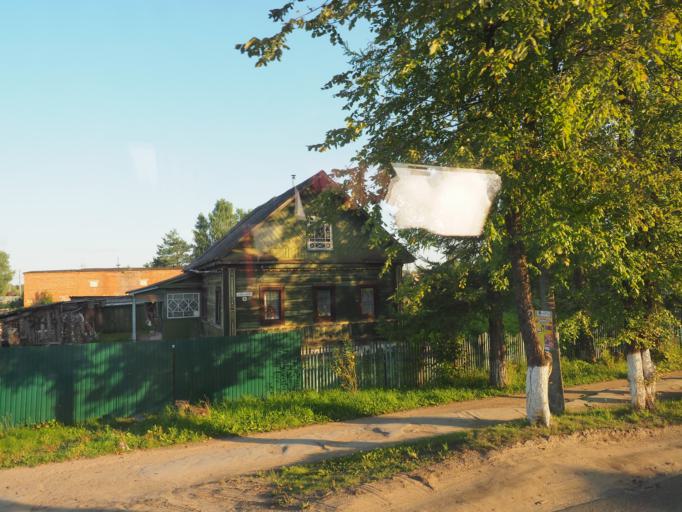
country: RU
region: Vologda
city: Chagoda
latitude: 59.1633
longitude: 35.3246
